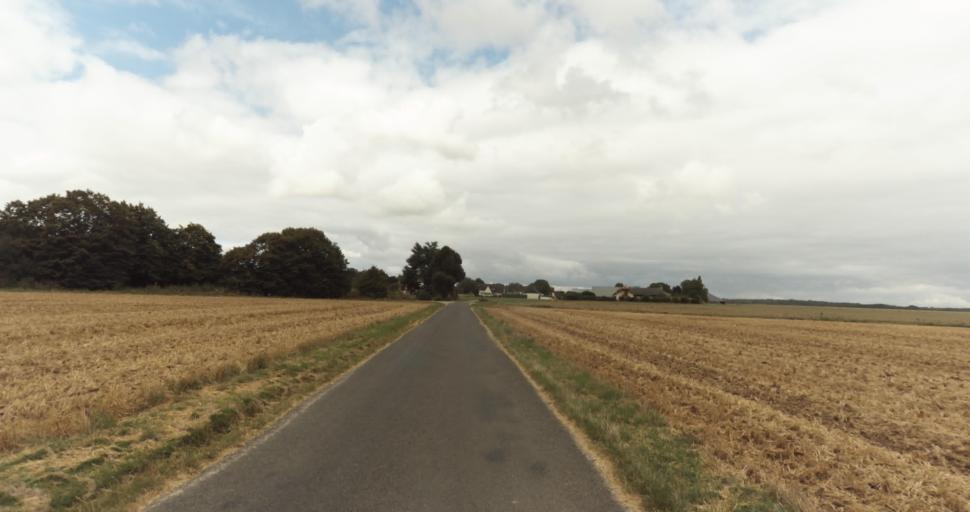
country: FR
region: Haute-Normandie
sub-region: Departement de l'Eure
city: Menilles
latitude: 49.0196
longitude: 1.2780
